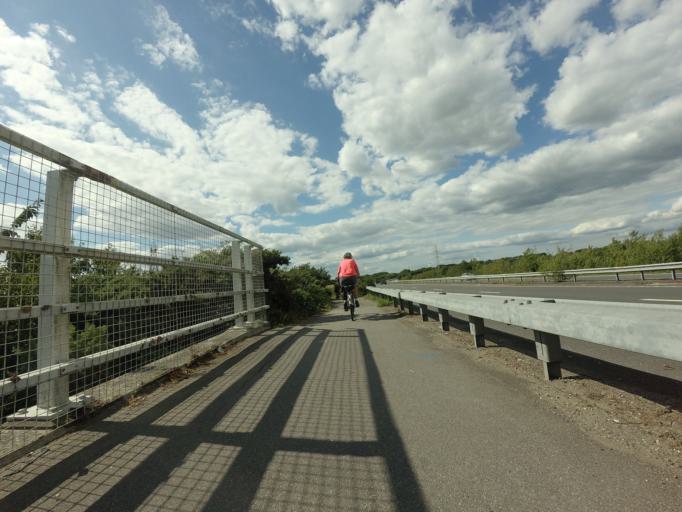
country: GB
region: England
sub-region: East Sussex
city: Eastbourne
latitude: 50.8099
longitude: 0.2791
